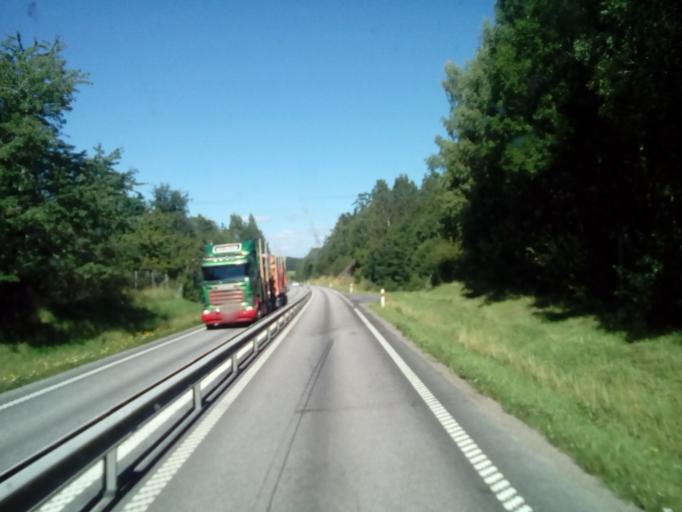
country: SE
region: OEstergoetland
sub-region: Kinda Kommun
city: Rimforsa
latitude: 58.1056
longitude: 15.6706
